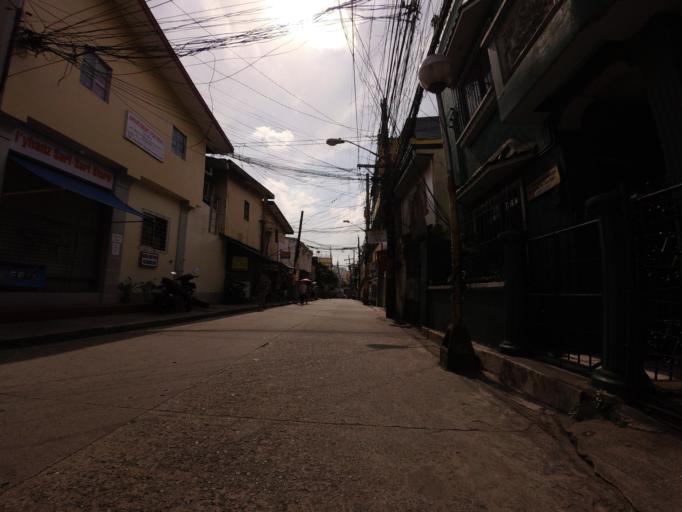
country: PH
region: Metro Manila
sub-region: San Juan
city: San Juan
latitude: 14.5899
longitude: 121.0270
